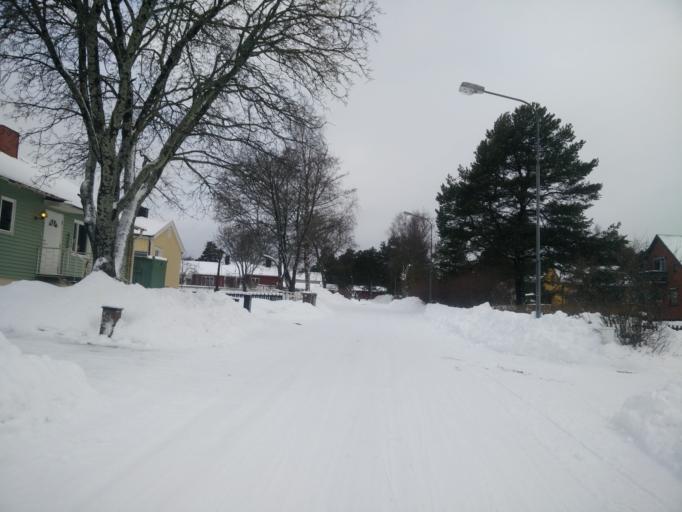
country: SE
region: Vaesternorrland
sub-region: Sundsvalls Kommun
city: Nolby
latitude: 62.2900
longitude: 17.3670
